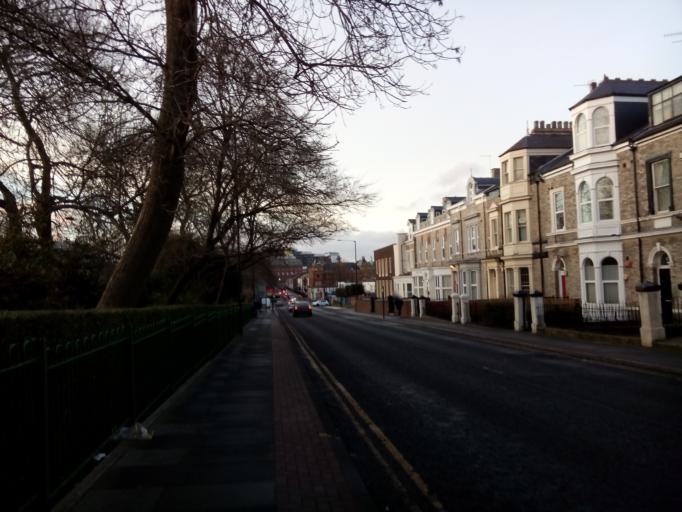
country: GB
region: England
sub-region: Sunderland
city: Sunderland
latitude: 54.9028
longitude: -1.3785
